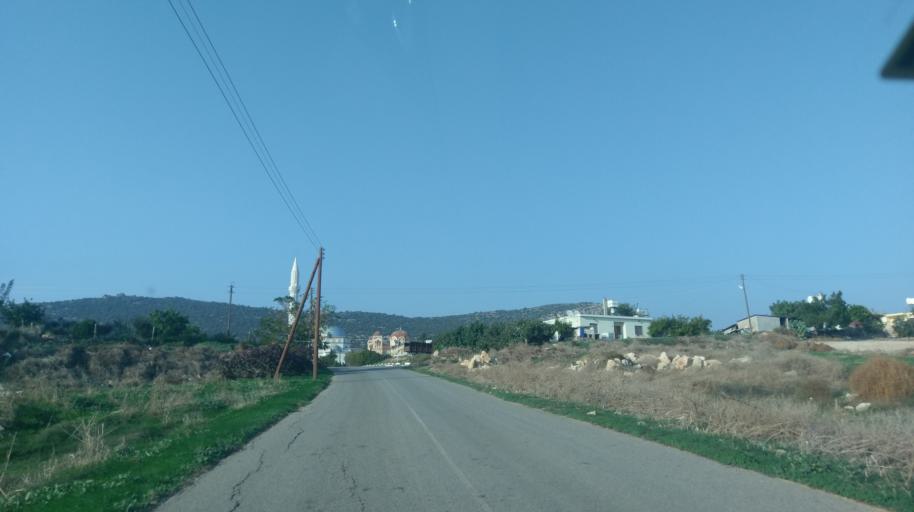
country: CY
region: Ammochostos
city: Leonarisso
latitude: 35.4419
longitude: 34.0315
